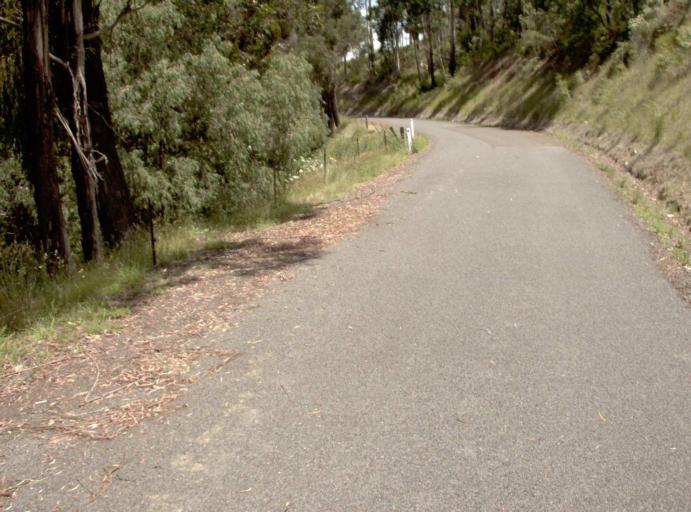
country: AU
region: New South Wales
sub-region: Bombala
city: Bombala
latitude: -37.3678
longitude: 149.0171
